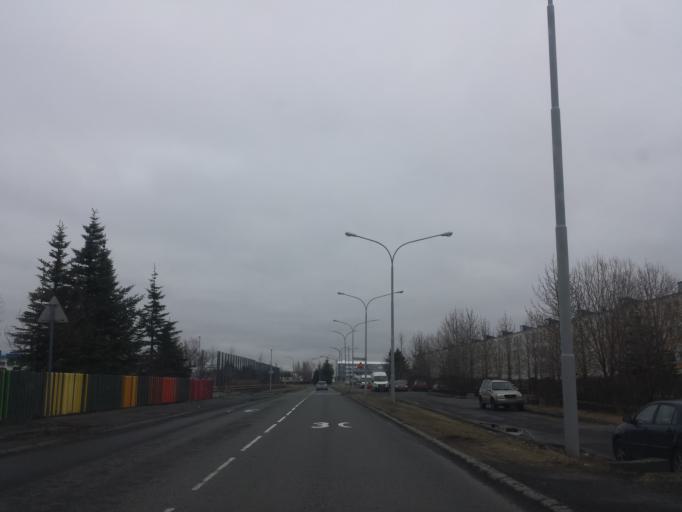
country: IS
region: Capital Region
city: Reykjavik
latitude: 64.1017
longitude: -21.8227
